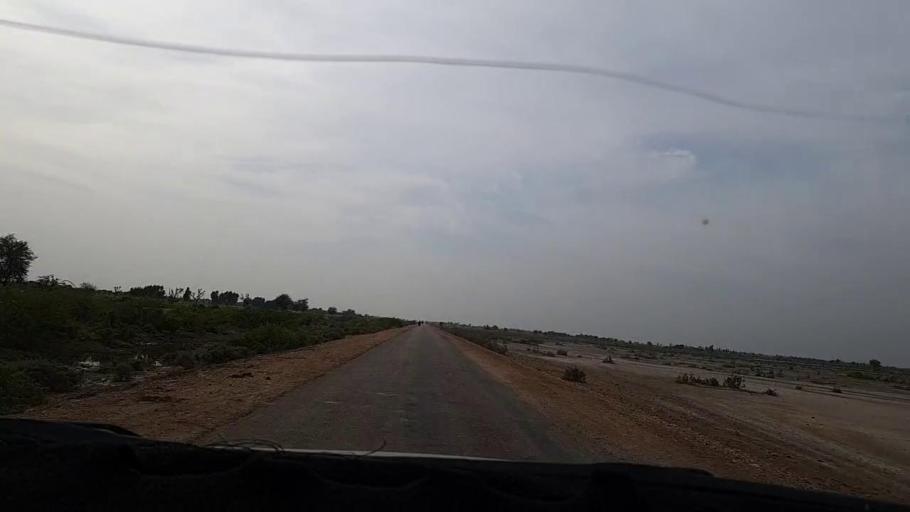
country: PK
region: Sindh
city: Pithoro
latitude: 25.5161
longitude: 69.2855
